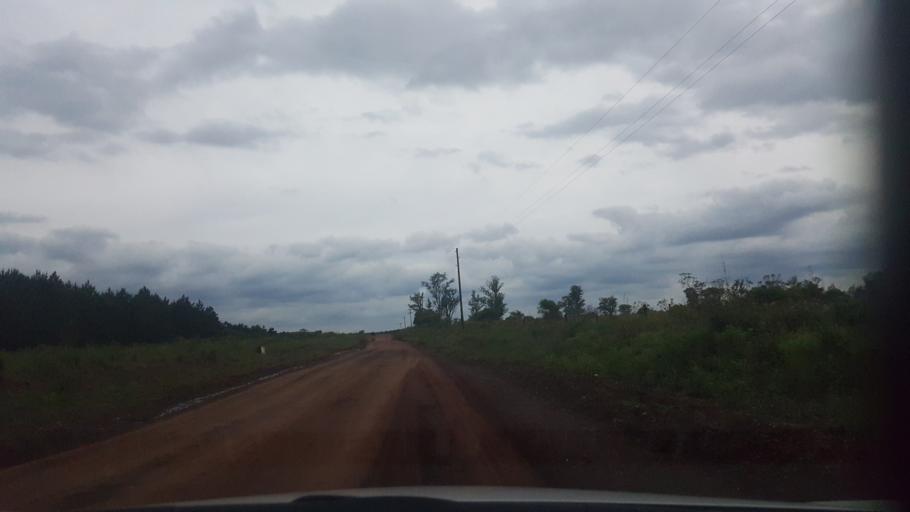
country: AR
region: Misiones
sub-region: Departamento de Candelaria
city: Candelaria
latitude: -27.4976
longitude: -55.7372
